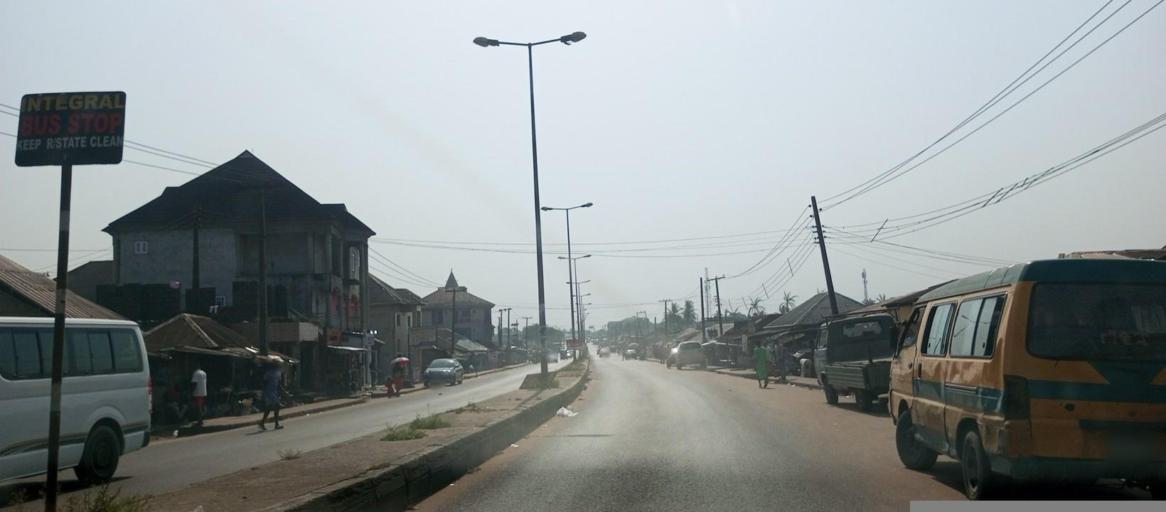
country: NG
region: Rivers
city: Emuoha
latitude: 4.8859
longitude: 6.9016
